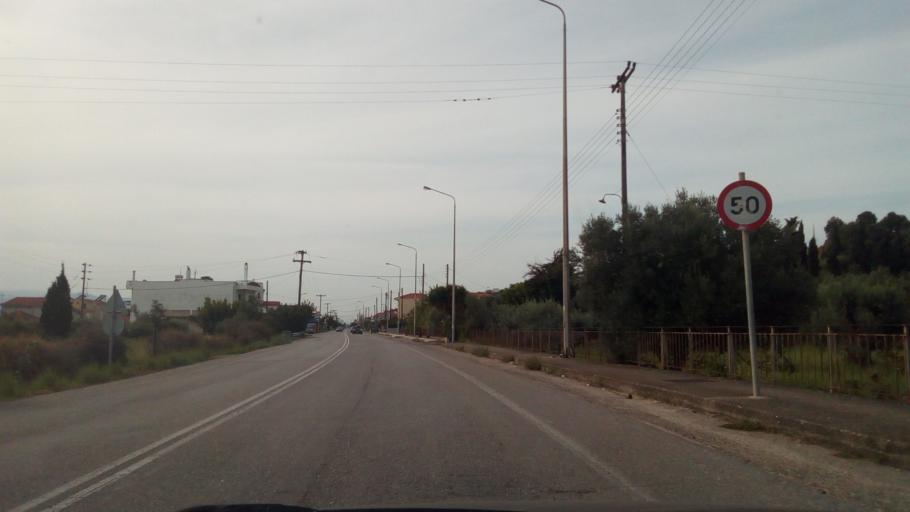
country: GR
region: West Greece
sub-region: Nomos Aitolias kai Akarnanias
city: Antirrio
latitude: 38.3676
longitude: 21.7796
